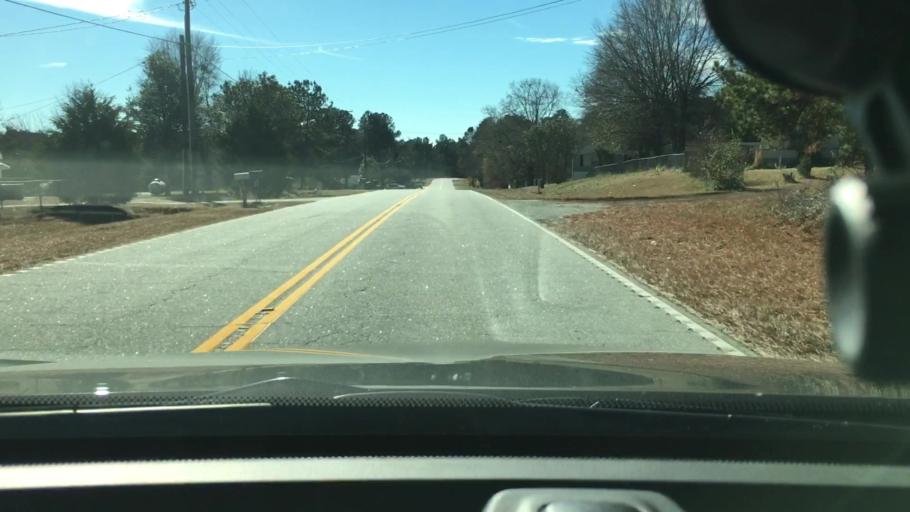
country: US
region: South Carolina
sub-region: Spartanburg County
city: Pacolet
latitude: 34.9415
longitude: -81.7202
